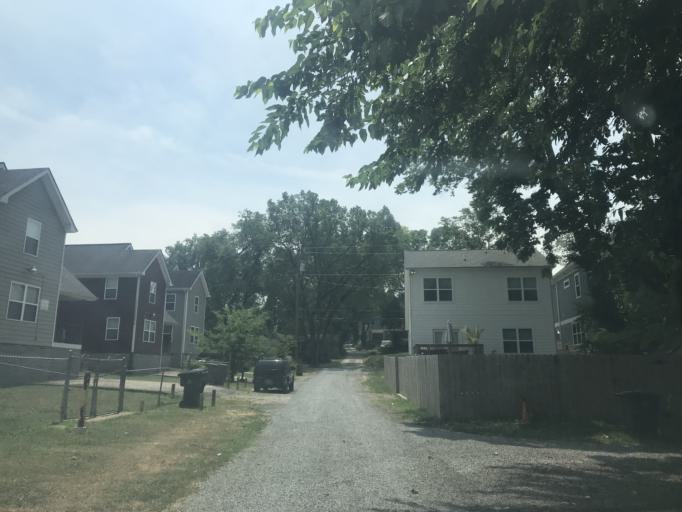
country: US
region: Tennessee
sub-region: Davidson County
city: Nashville
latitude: 36.1892
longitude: -86.8128
